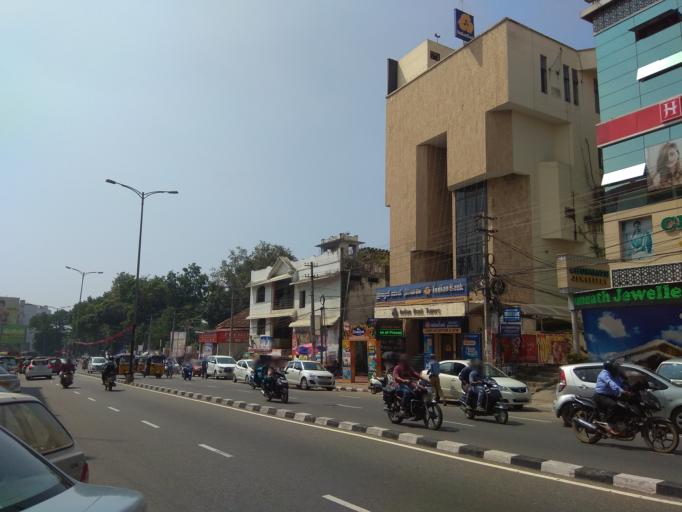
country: IN
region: Kerala
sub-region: Thiruvananthapuram
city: Thiruvananthapuram
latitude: 8.4929
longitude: 76.9476
